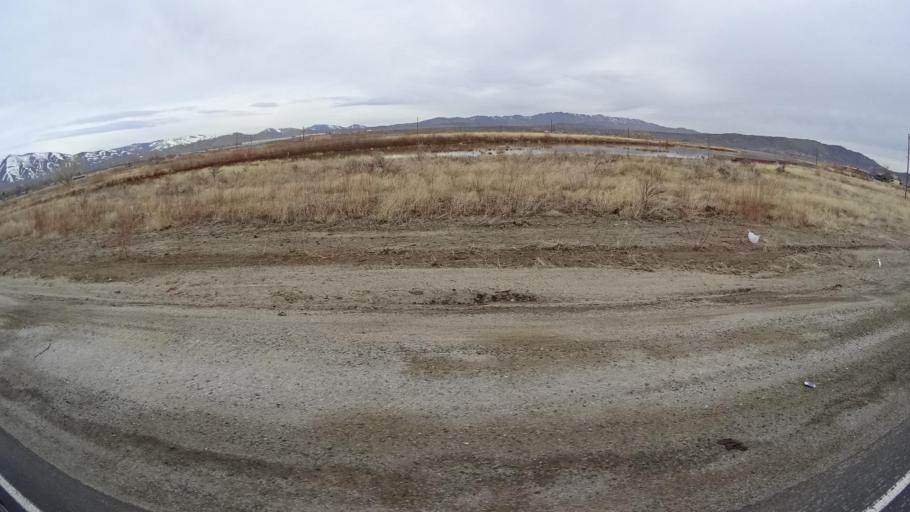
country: US
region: Nevada
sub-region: Washoe County
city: Lemmon Valley
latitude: 39.6482
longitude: -119.8290
